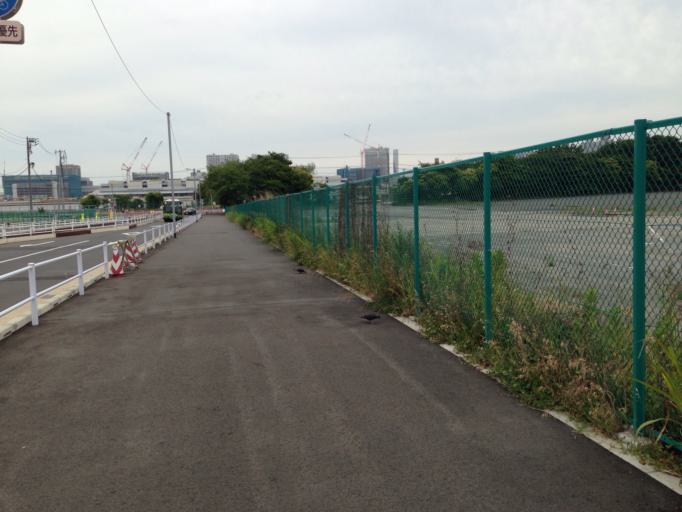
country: JP
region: Tokyo
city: Tokyo
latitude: 35.6503
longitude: 139.7745
